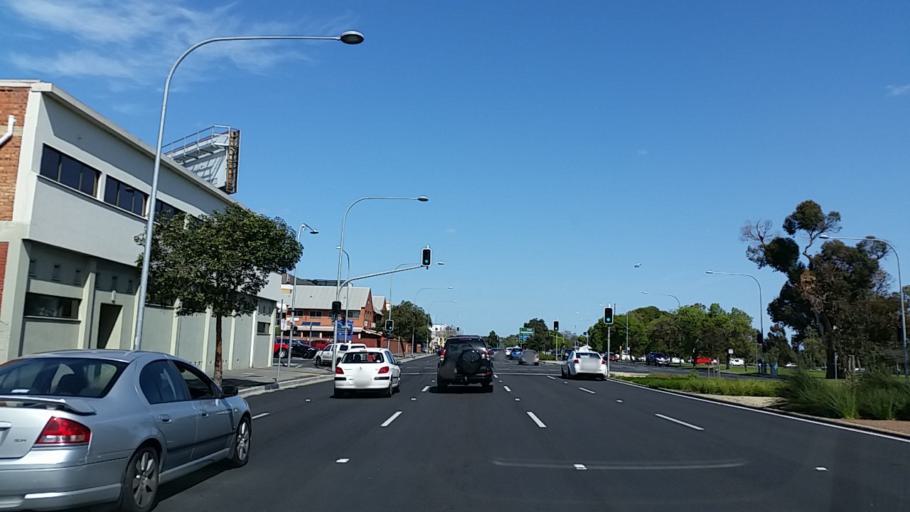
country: AU
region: South Australia
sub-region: Adelaide
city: Adelaide
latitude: -34.9272
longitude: 138.5878
